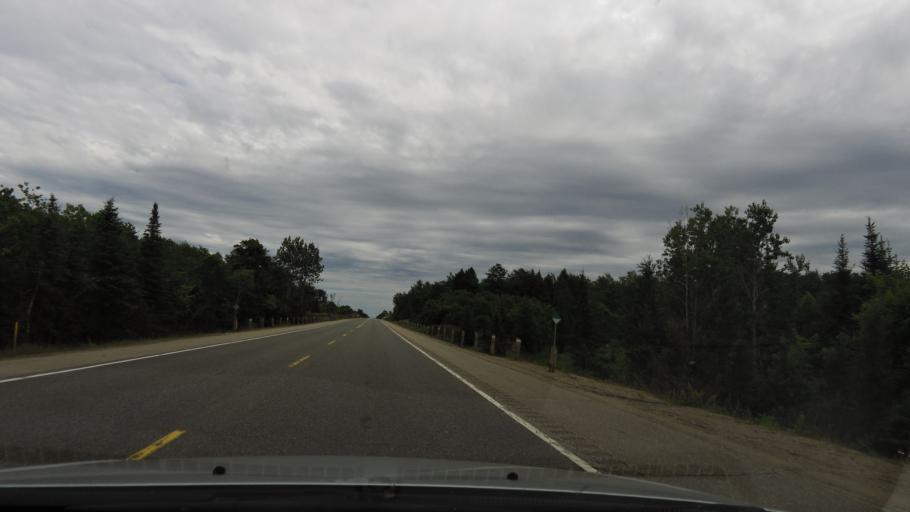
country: CA
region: Ontario
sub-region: Parry Sound District
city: Parry Sound
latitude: 45.5372
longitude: -80.2640
